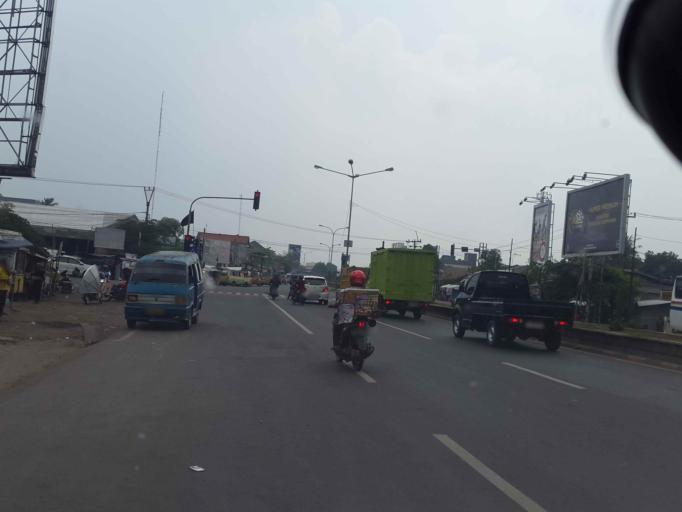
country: ID
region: West Java
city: Cikarang
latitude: -6.2743
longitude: 107.2704
